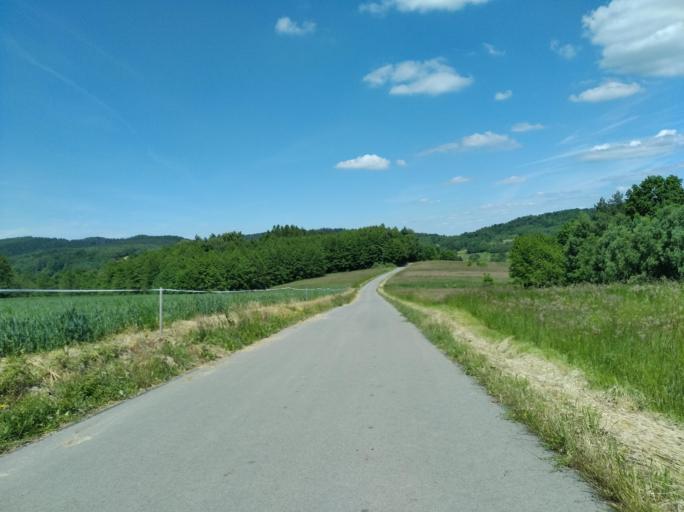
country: PL
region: Subcarpathian Voivodeship
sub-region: Powiat krosnienski
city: Wojaszowka
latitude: 49.7874
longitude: 21.7168
